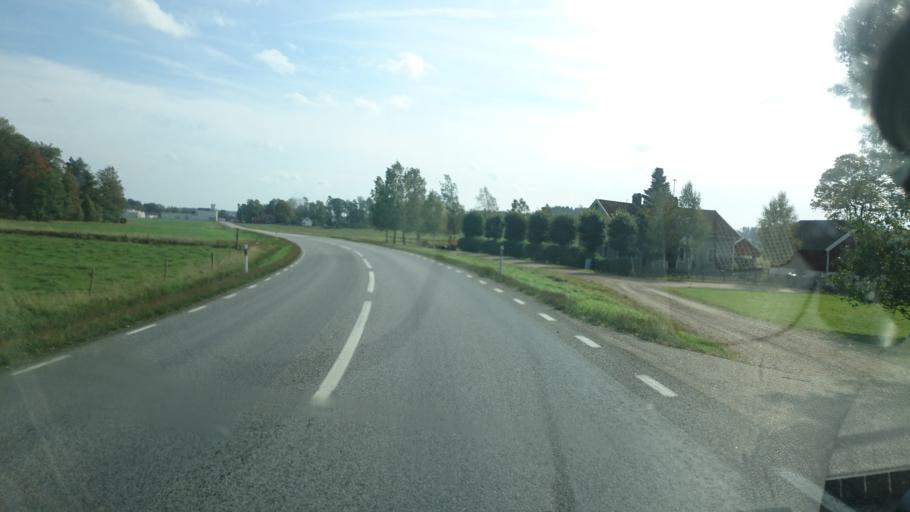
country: SE
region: Vaestra Goetaland
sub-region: Alingsas Kommun
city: Sollebrunn
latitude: 58.1247
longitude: 12.5043
